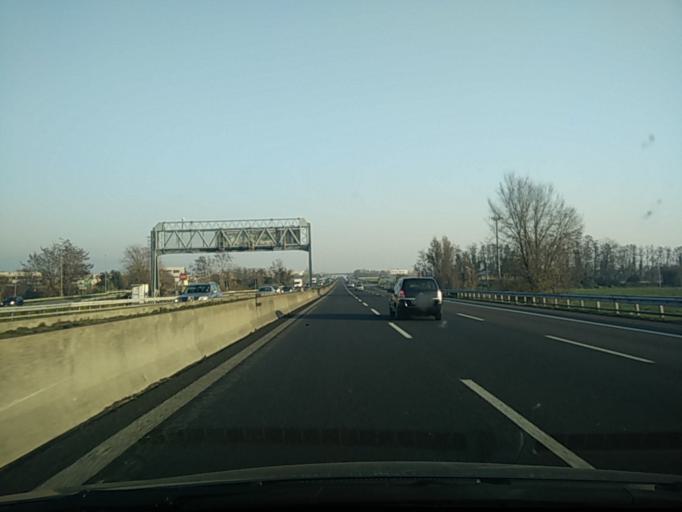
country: IT
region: Lombardy
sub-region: Provincia di Bergamo
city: Grumello del Monte
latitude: 45.6301
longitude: 9.8686
